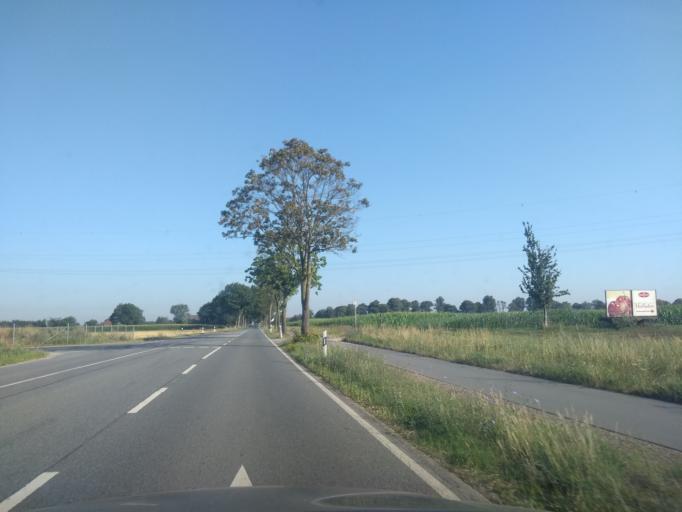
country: DE
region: North Rhine-Westphalia
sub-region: Regierungsbezirk Dusseldorf
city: Kleve
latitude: 51.8179
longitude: 6.1173
